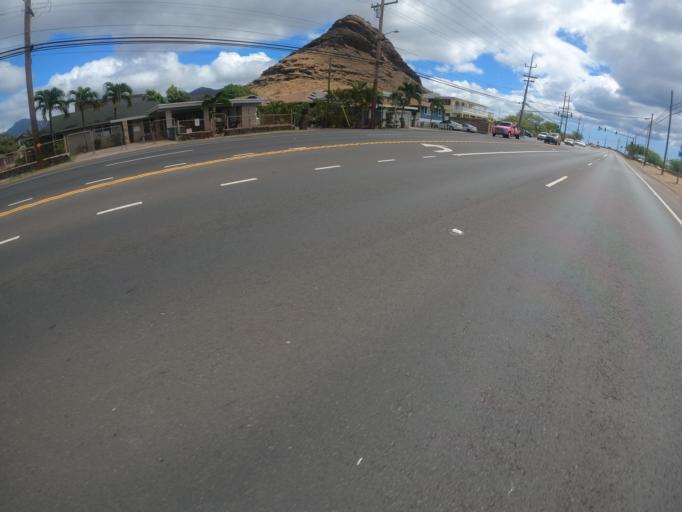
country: US
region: Hawaii
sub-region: Honolulu County
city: Ma'ili
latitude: 21.4046
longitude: -158.1769
